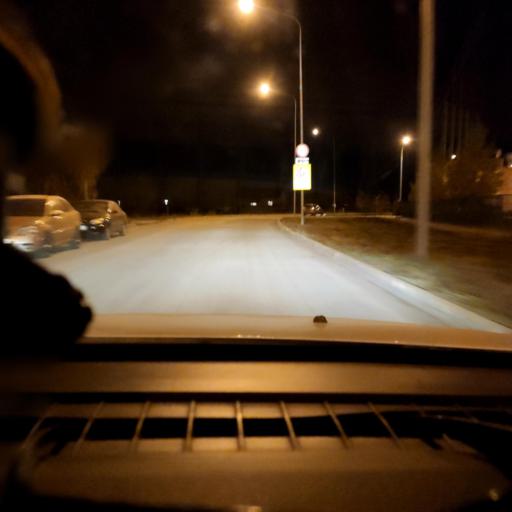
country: RU
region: Samara
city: Samara
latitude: 53.1118
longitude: 50.1380
